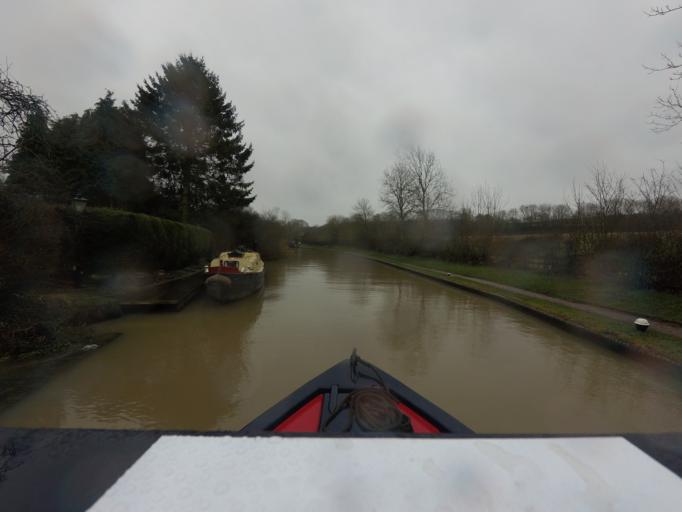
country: GB
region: England
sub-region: Northamptonshire
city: Daventry
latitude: 52.2882
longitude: -1.1965
